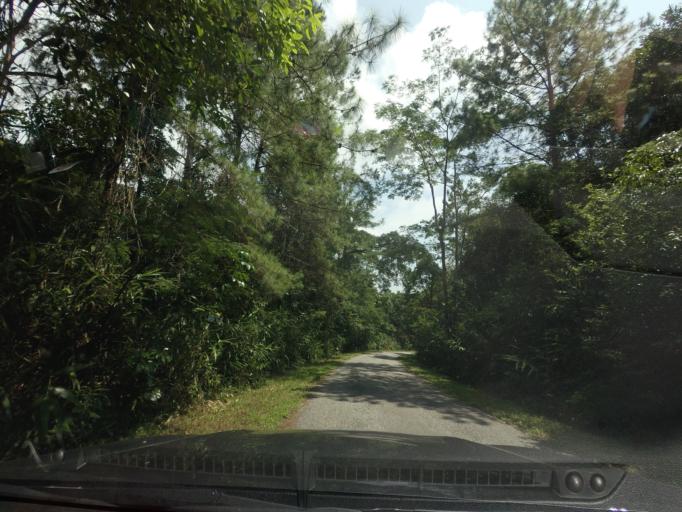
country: TH
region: Loei
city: Phu Ruea
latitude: 17.4921
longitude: 101.3504
